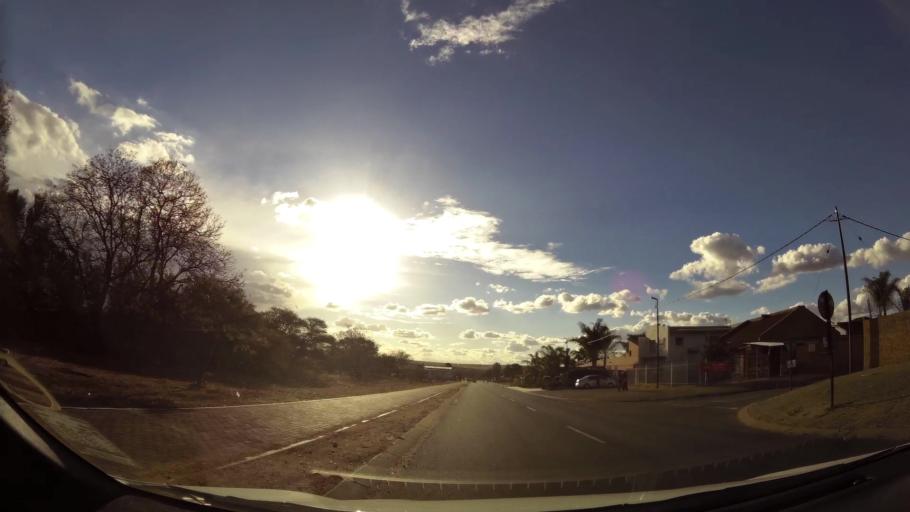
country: ZA
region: Limpopo
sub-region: Capricorn District Municipality
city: Polokwane
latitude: -23.9191
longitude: 29.4304
